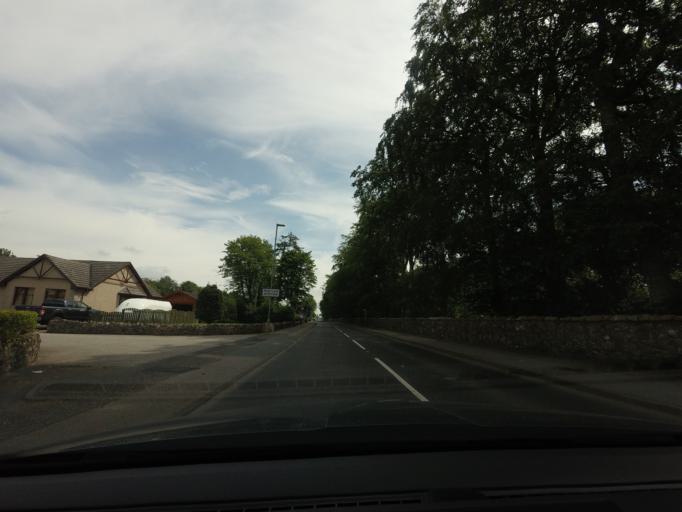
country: GB
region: Scotland
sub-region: Aberdeenshire
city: Mintlaw
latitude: 57.5260
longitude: -2.0243
